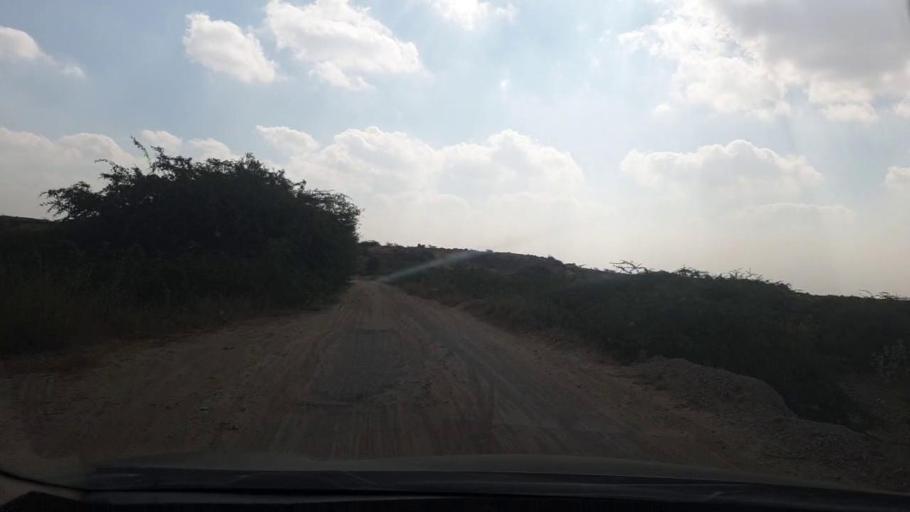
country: PK
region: Sindh
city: Malir Cantonment
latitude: 25.0260
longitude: 67.3493
